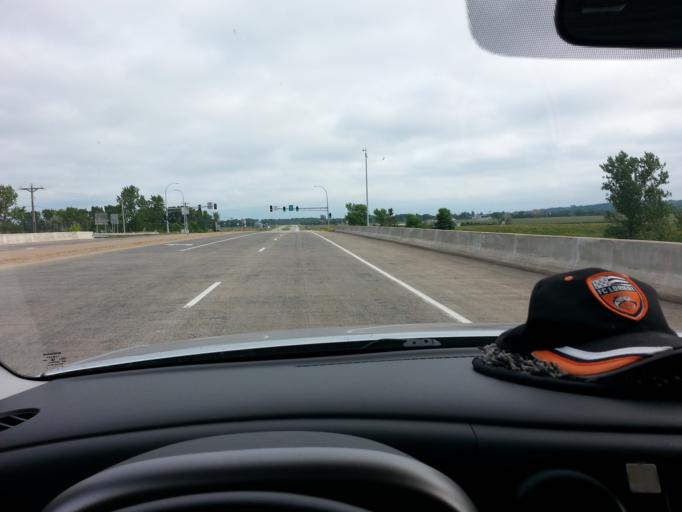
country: US
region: Minnesota
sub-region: Washington County
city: Lake Elmo
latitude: 44.9484
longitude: -92.8624
